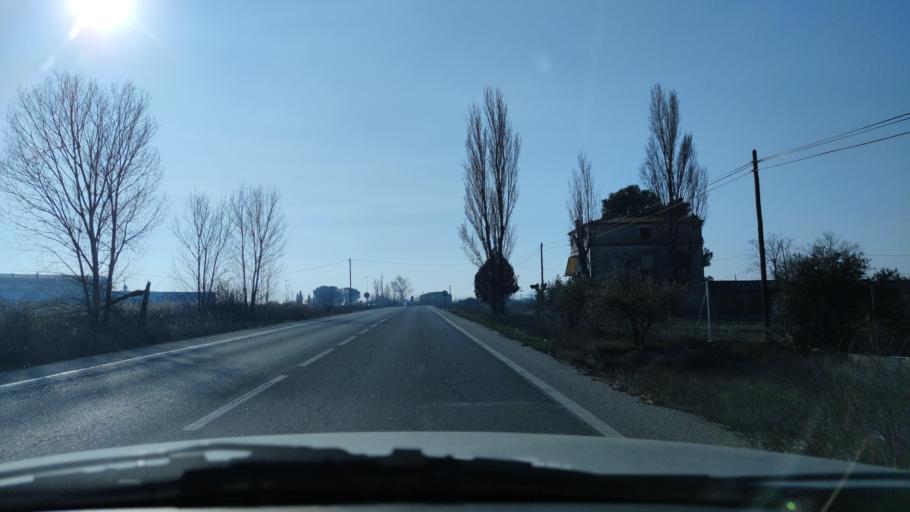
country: ES
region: Catalonia
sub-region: Provincia de Lleida
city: Lleida
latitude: 41.6486
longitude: 0.6351
